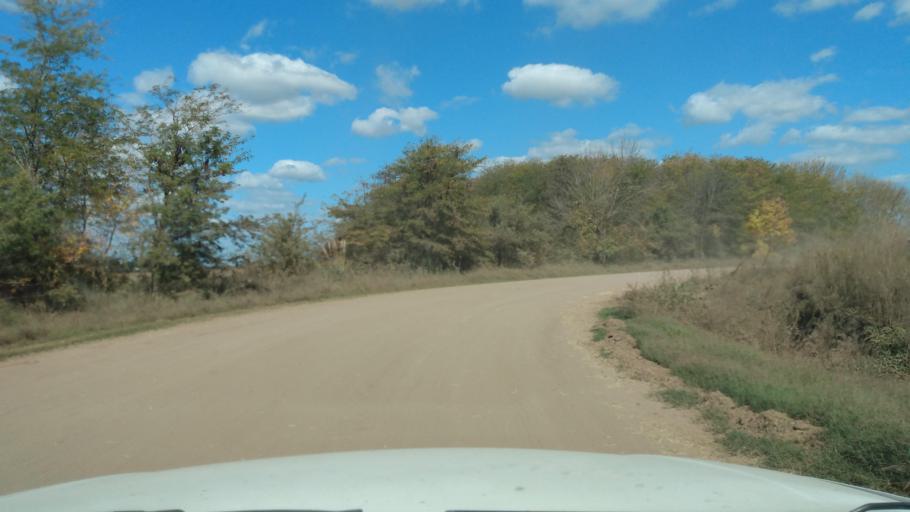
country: AR
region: Buenos Aires
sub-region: Partido de Navarro
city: Navarro
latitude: -35.0173
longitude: -59.4242
